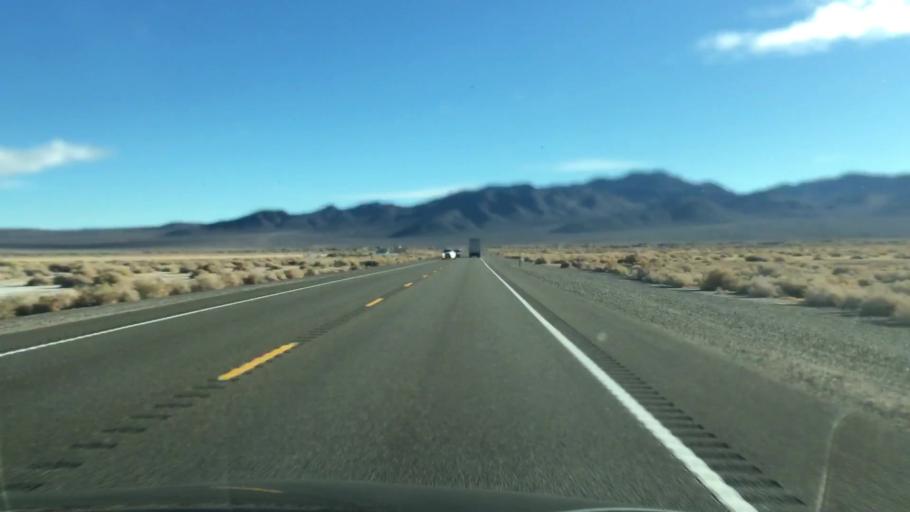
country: US
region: Nevada
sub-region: Mineral County
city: Hawthorne
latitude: 38.2763
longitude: -118.0989
